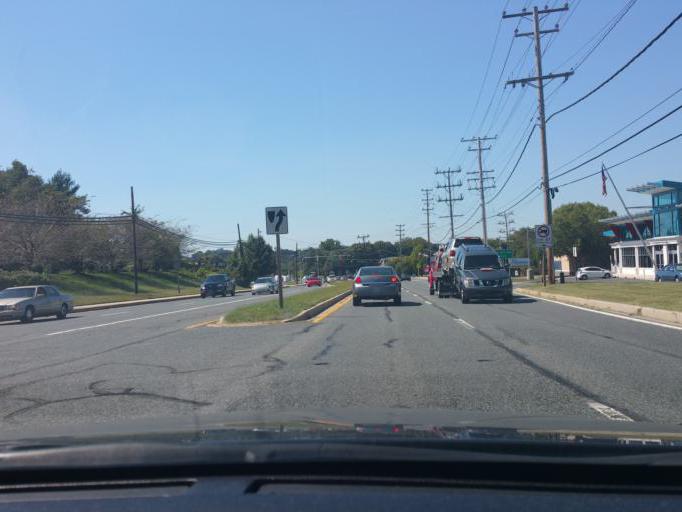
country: US
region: Maryland
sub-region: Harford County
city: South Bel Air
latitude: 39.5451
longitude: -76.3218
